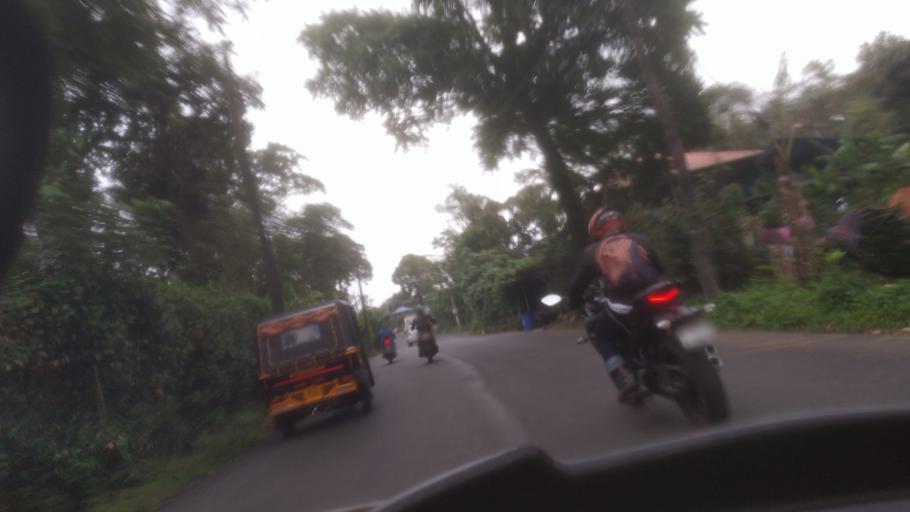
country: IN
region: Tamil Nadu
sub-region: Theni
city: Kombai
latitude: 9.8911
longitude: 77.1528
